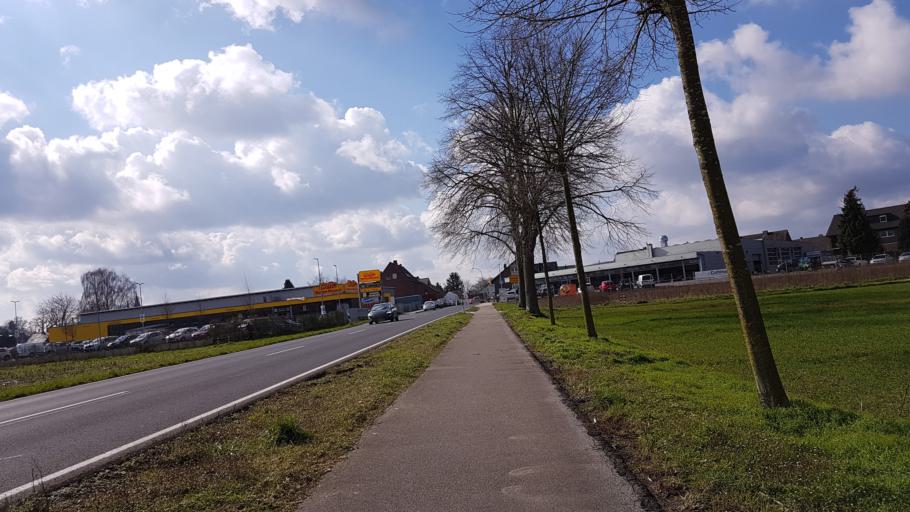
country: DE
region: North Rhine-Westphalia
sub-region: Regierungsbezirk Dusseldorf
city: Niederkruchten
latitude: 51.2037
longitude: 6.2215
